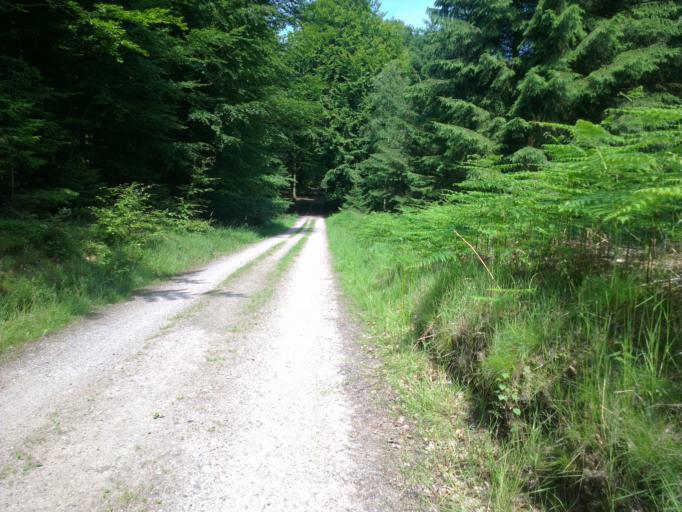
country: DK
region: Capital Region
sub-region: Allerod Kommune
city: Lillerod
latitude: 55.9072
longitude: 12.3652
